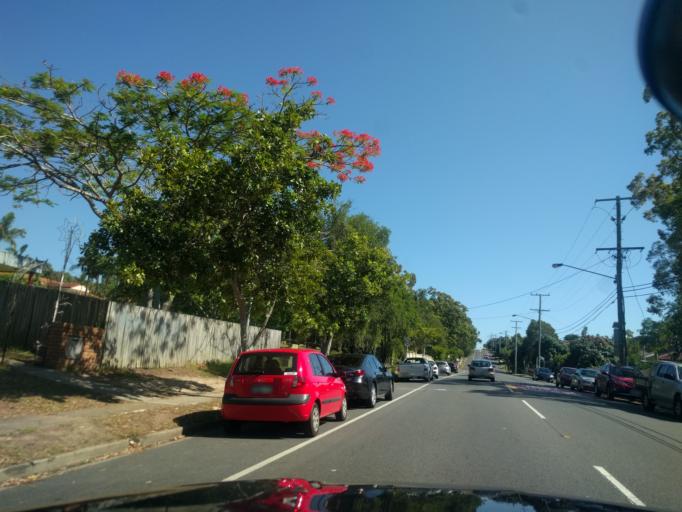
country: AU
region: Queensland
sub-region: Brisbane
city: Chermside West
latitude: -27.3806
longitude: 153.0133
